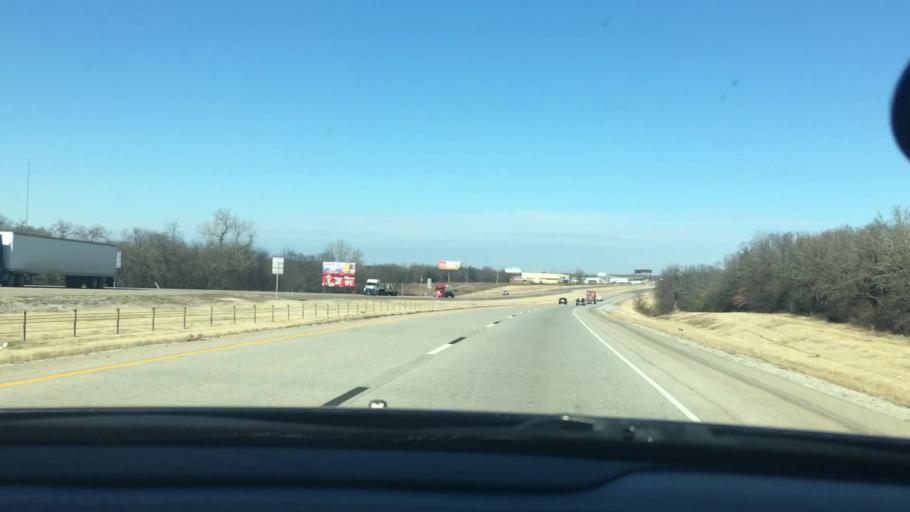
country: US
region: Oklahoma
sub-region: Carter County
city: Ardmore
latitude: 34.1595
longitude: -97.1639
